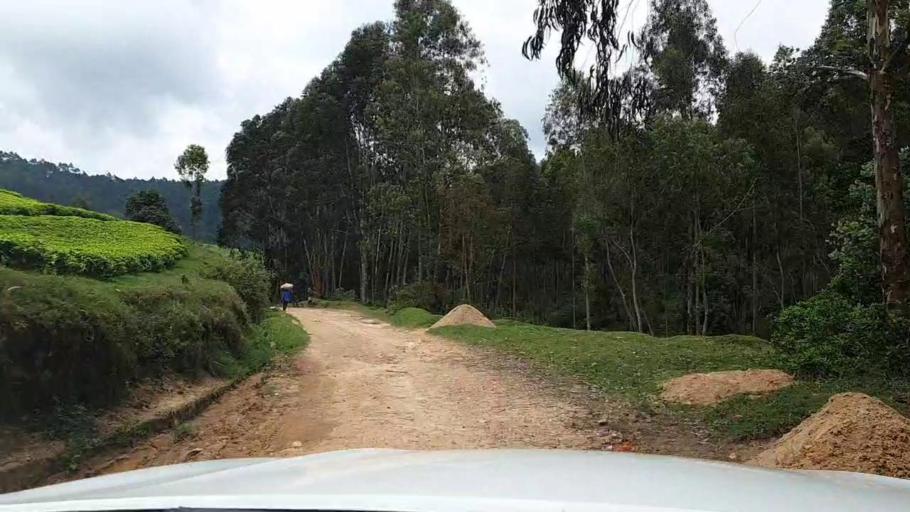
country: RW
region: Western Province
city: Kibuye
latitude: -2.2787
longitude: 29.3661
